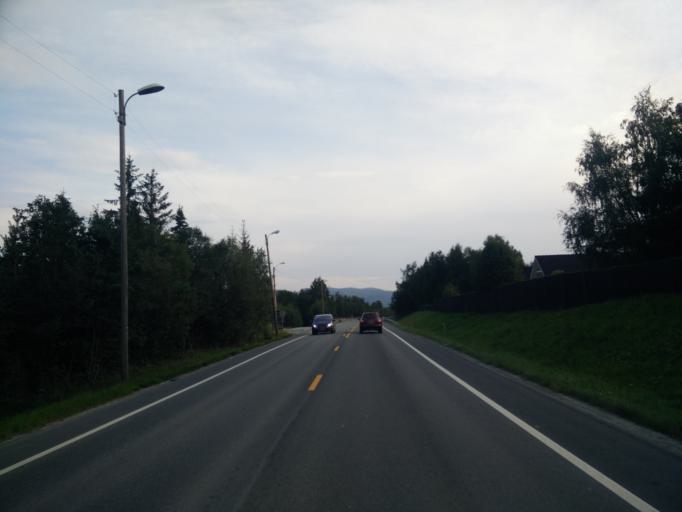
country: NO
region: Sor-Trondelag
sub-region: Trondheim
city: Trondheim
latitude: 63.3493
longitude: 10.3694
